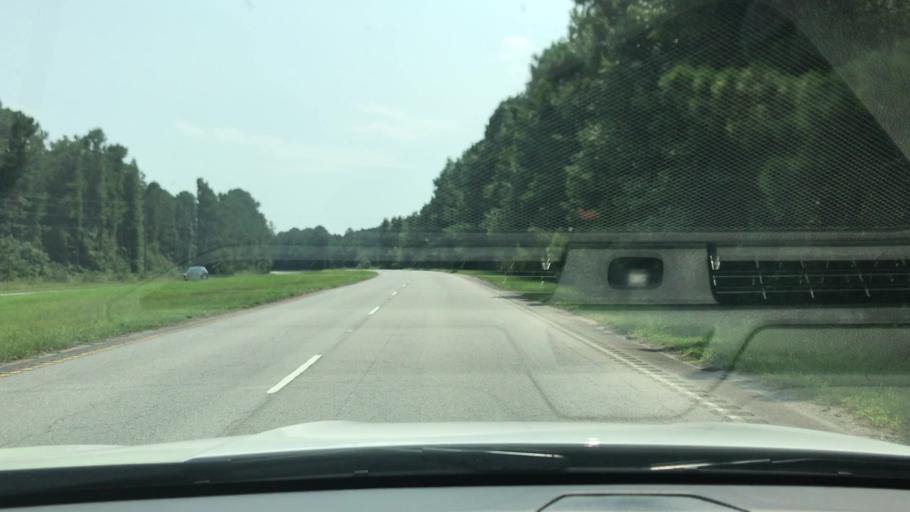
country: US
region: South Carolina
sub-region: Charleston County
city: Awendaw
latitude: 33.0044
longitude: -79.6426
